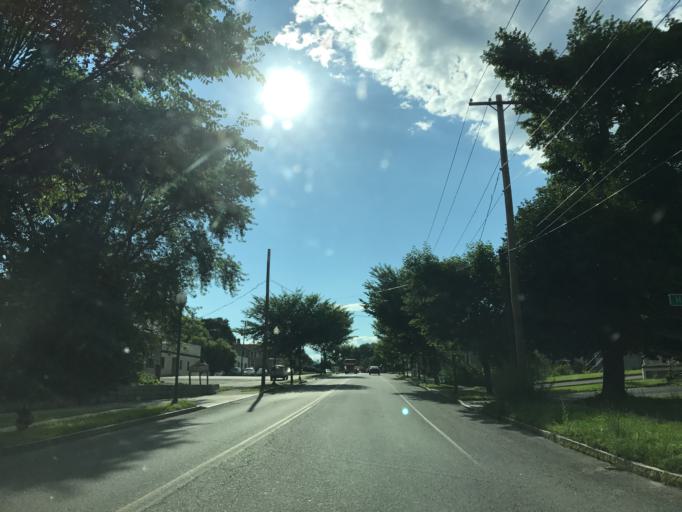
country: US
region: New York
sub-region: Saratoga County
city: South Glens Falls
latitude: 43.3099
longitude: -73.6250
